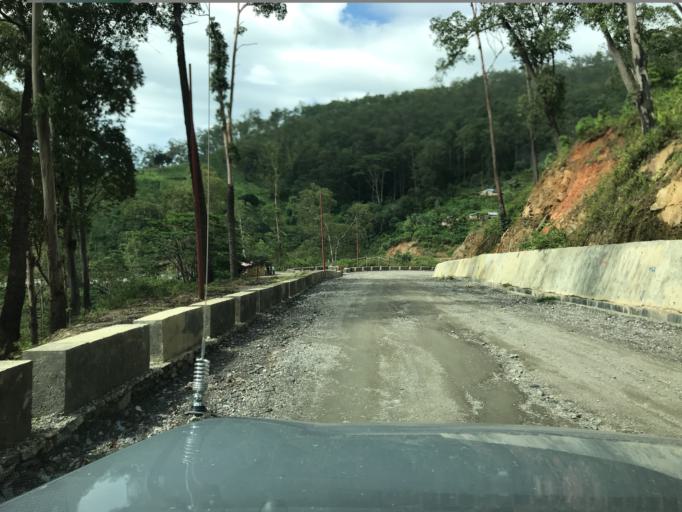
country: TL
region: Aileu
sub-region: Aileu Villa
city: Aileu
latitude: -8.6616
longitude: 125.5316
